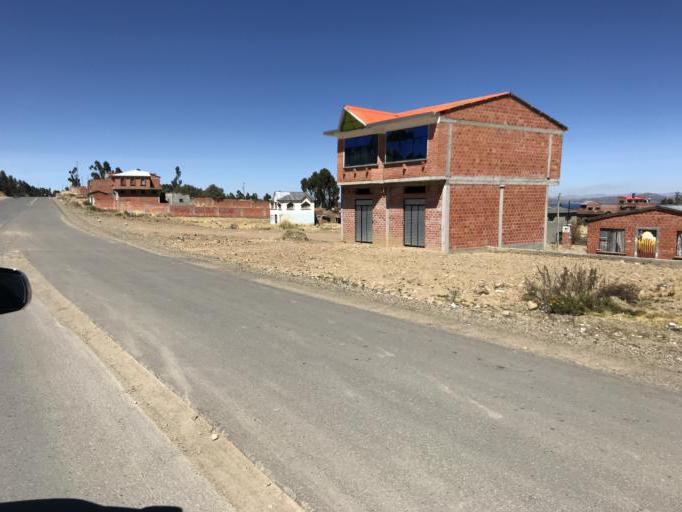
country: BO
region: La Paz
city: Huatajata
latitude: -16.1953
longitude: -68.7210
